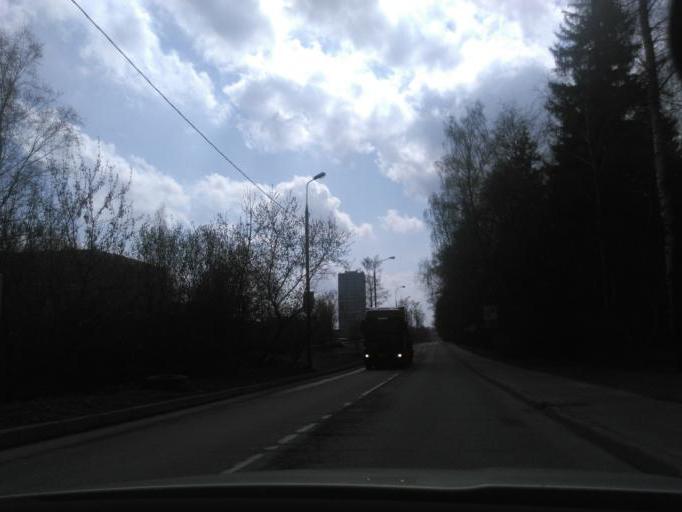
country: RU
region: Moskovskaya
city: Mendeleyevo
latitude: 56.0187
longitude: 37.1957
